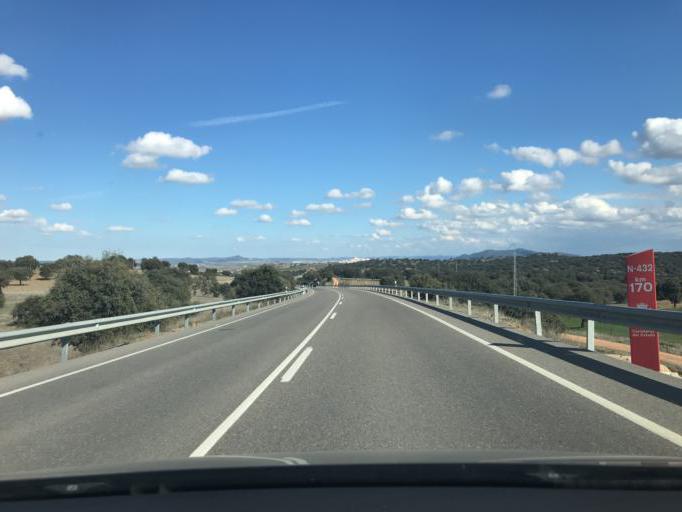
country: ES
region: Andalusia
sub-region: Province of Cordoba
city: Fuente Obejuna
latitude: 38.2590
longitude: -5.4699
